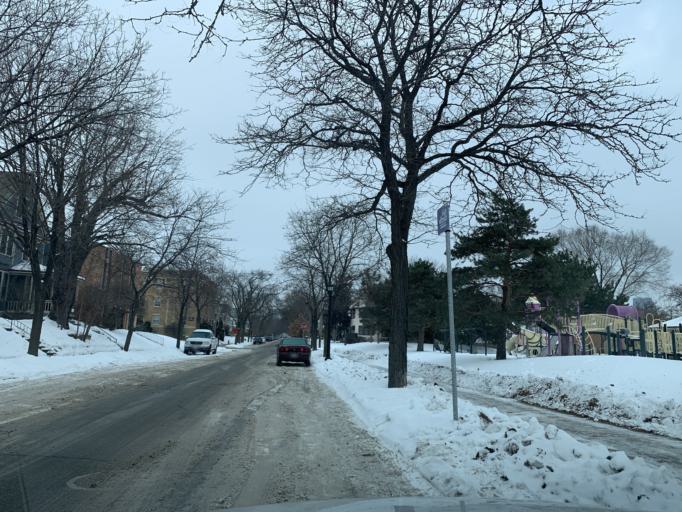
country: US
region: Minnesota
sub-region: Hennepin County
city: Minneapolis
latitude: 44.9567
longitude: -93.2918
